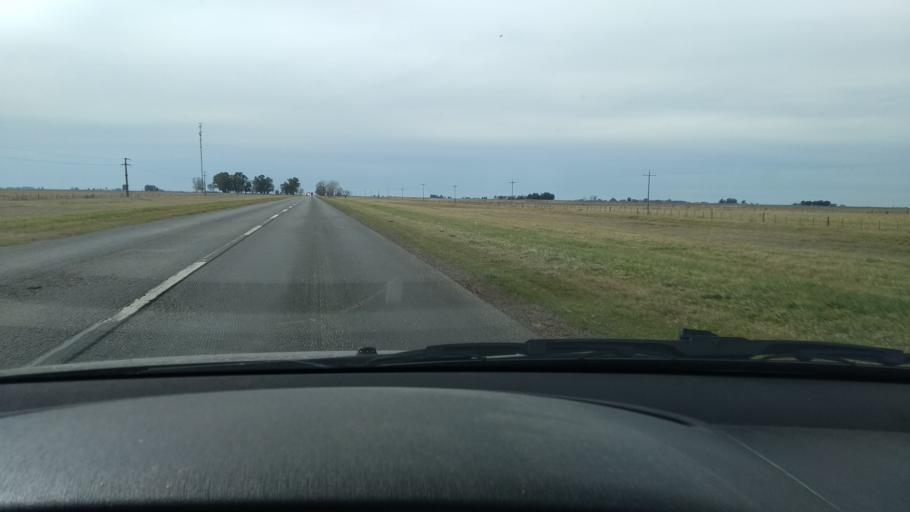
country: AR
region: Buenos Aires
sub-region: Partido de Azul
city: Azul
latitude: -36.7381
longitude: -59.7882
